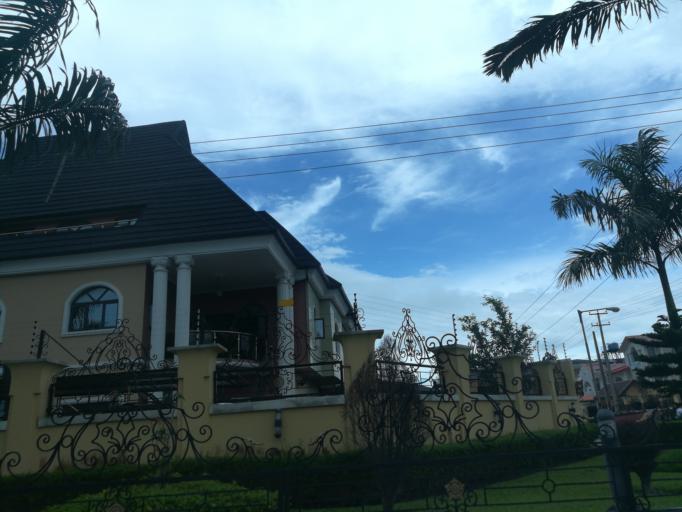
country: NG
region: Lagos
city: Ikoyi
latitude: 6.4467
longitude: 3.4767
